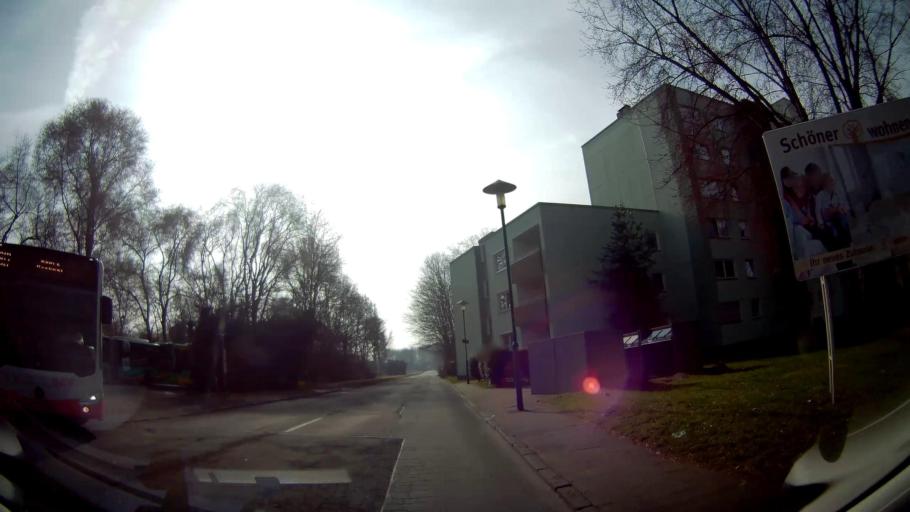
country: DE
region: North Rhine-Westphalia
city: Meiderich
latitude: 51.4990
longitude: 6.8158
